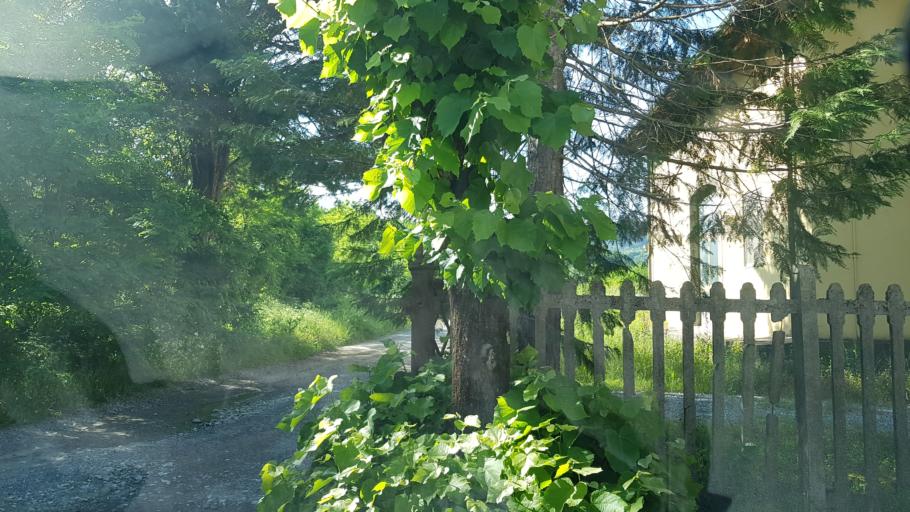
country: IT
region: Tuscany
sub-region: Provincia di Lucca
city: Camporgiano
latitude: 44.1613
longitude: 10.3345
